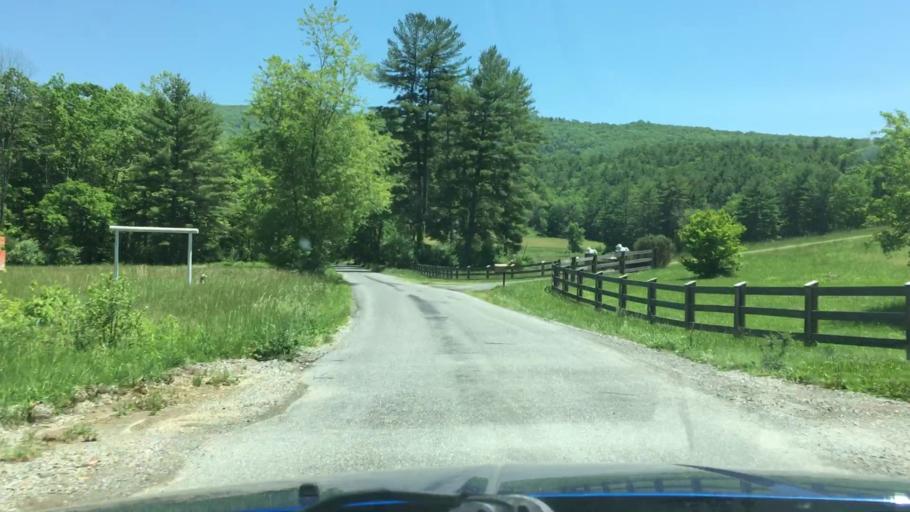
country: US
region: Virginia
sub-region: Bath County
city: Warm Springs
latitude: 38.0741
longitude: -79.5835
